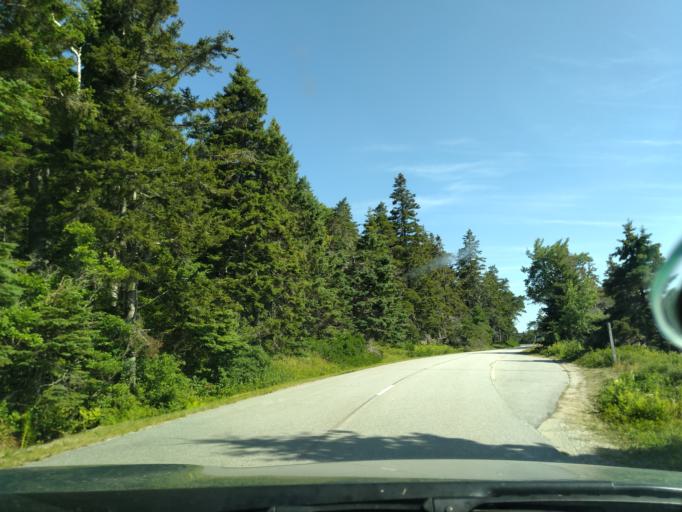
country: US
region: Maine
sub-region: Hancock County
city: Gouldsboro
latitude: 44.3485
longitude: -68.0464
